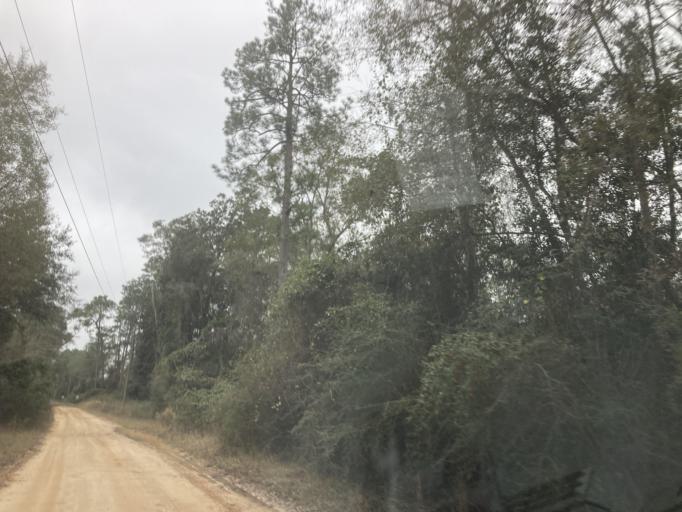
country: US
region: Mississippi
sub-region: Jackson County
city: Latimer
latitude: 30.6791
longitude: -88.9134
